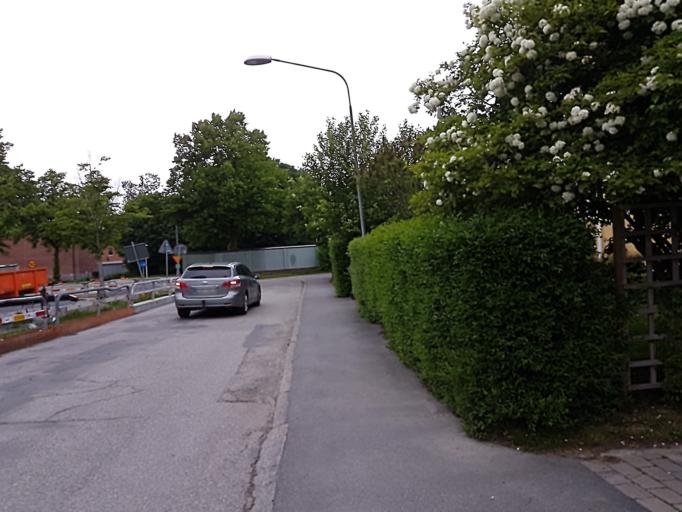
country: SE
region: Stockholm
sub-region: Stockholms Kommun
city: Arsta
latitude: 59.2870
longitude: 18.0837
